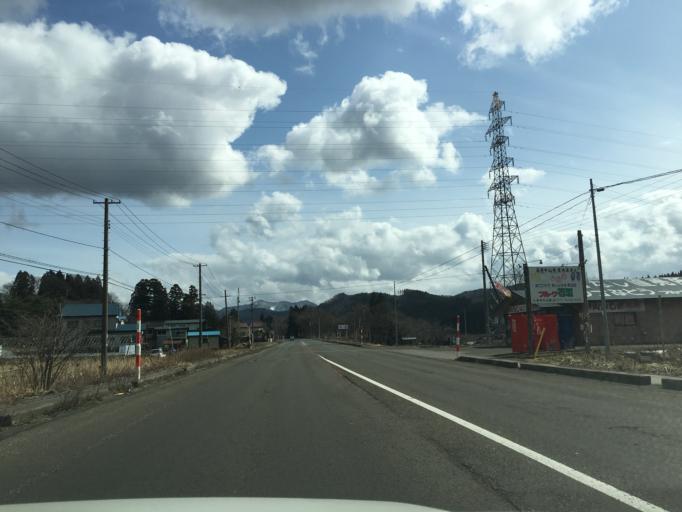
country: JP
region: Akita
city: Odate
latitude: 40.2271
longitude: 140.5995
